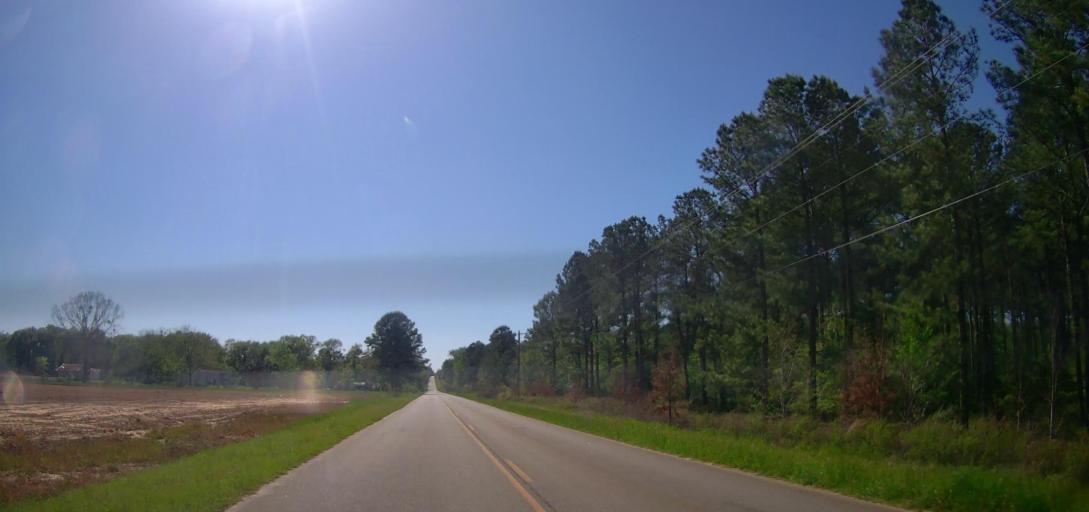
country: US
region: Georgia
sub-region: Pulaski County
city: Hawkinsville
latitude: 32.2405
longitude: -83.5324
